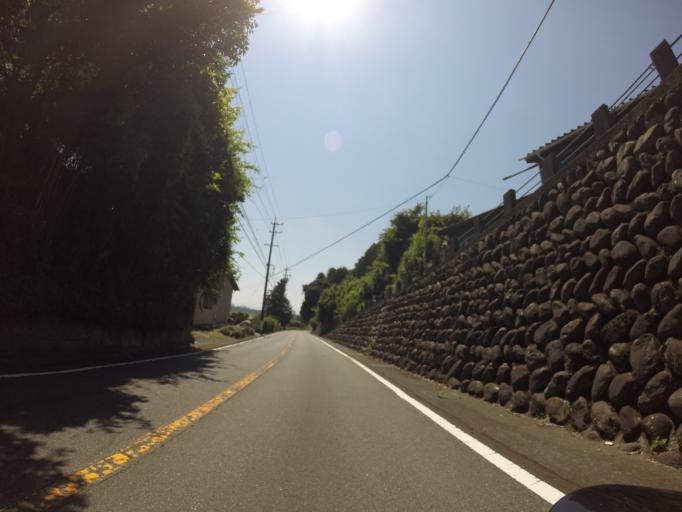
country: JP
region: Shizuoka
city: Fujinomiya
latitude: 35.1711
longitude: 138.6167
